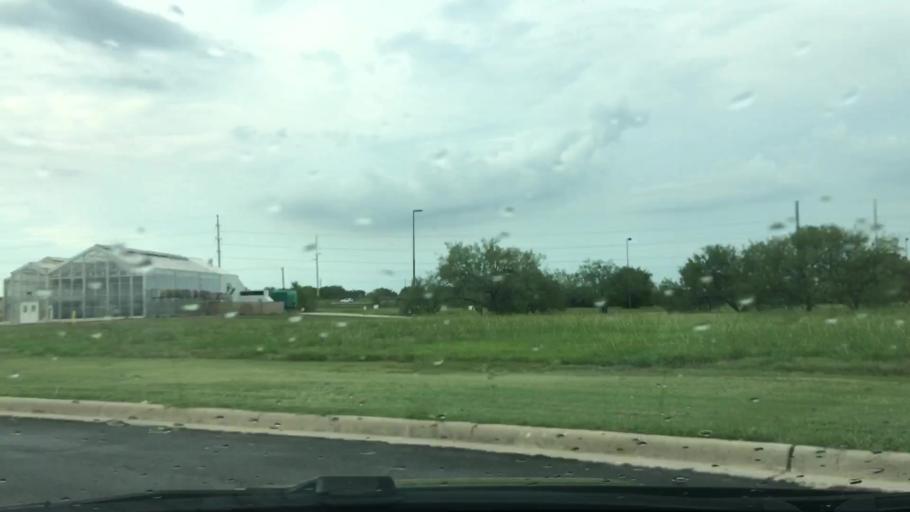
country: US
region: Texas
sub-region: Denton County
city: Denton
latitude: 33.2550
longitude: -97.1491
